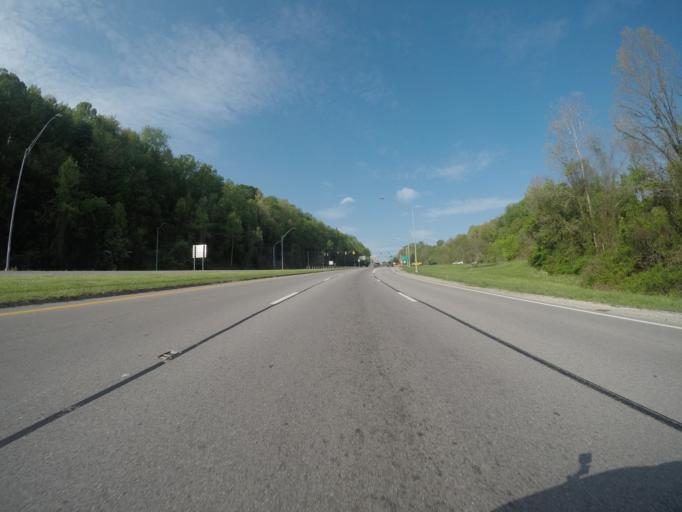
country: US
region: West Virginia
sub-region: Kanawha County
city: Charleston
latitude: 38.3470
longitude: -81.6522
